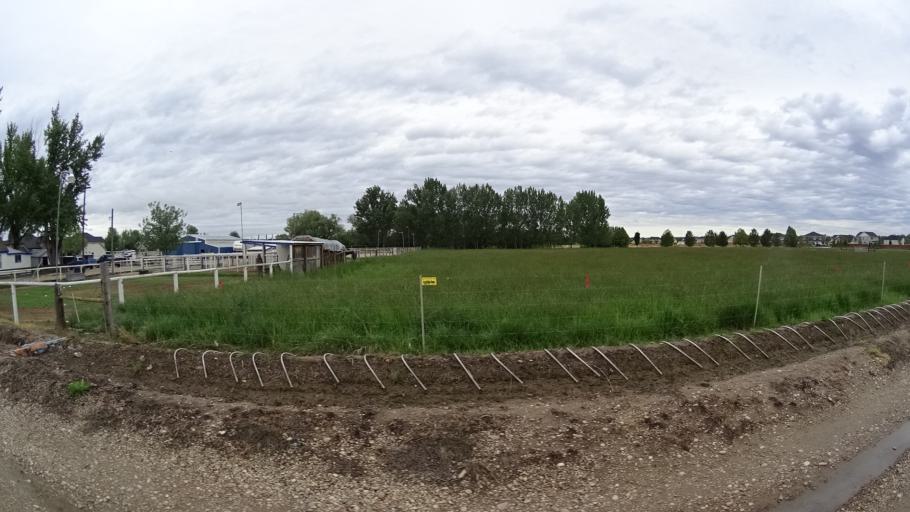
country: US
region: Idaho
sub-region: Ada County
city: Star
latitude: 43.6995
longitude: -116.4729
